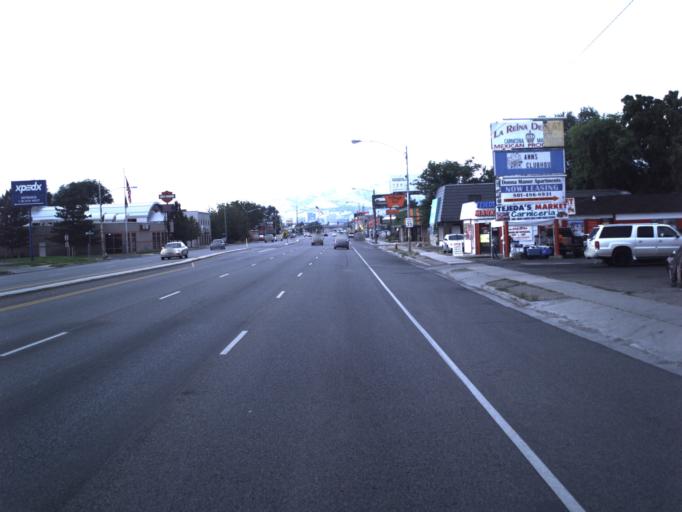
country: US
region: Utah
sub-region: Salt Lake County
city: South Salt Lake
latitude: 40.7062
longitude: -111.8882
